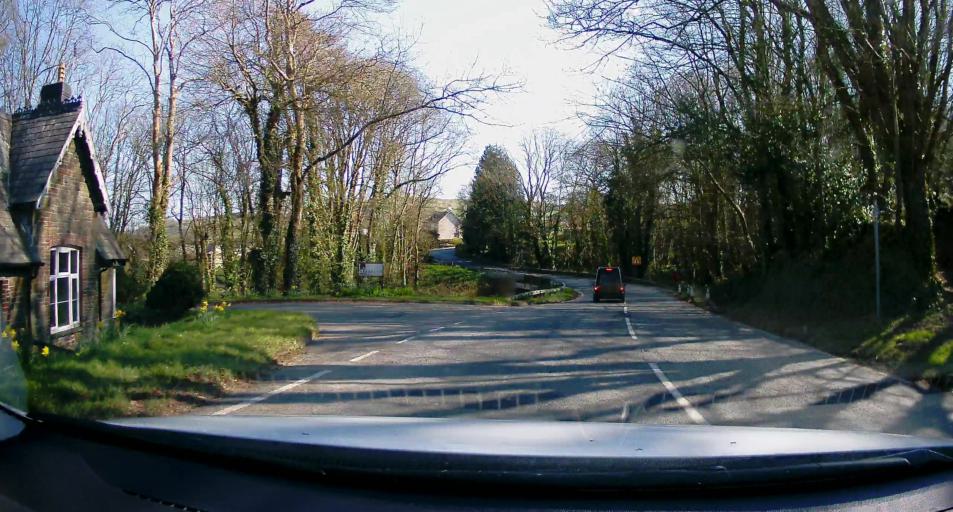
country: GB
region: Wales
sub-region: County of Ceredigion
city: Penparcau
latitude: 52.3628
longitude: -4.0585
